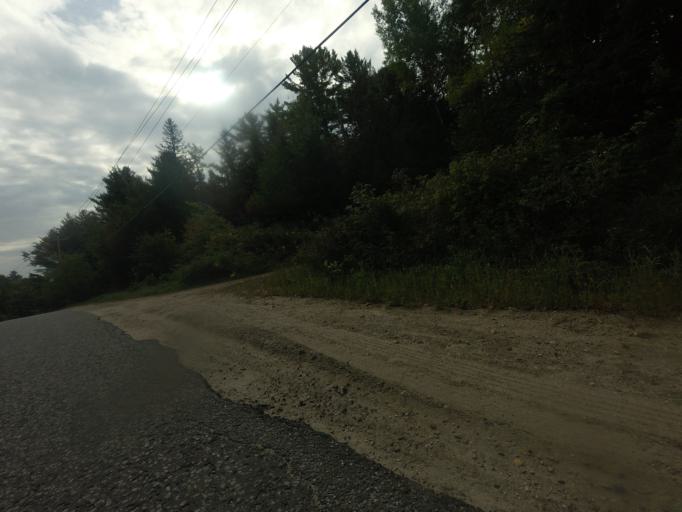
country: CA
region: Quebec
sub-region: Outaouais
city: Wakefield
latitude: 45.9705
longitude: -75.9361
